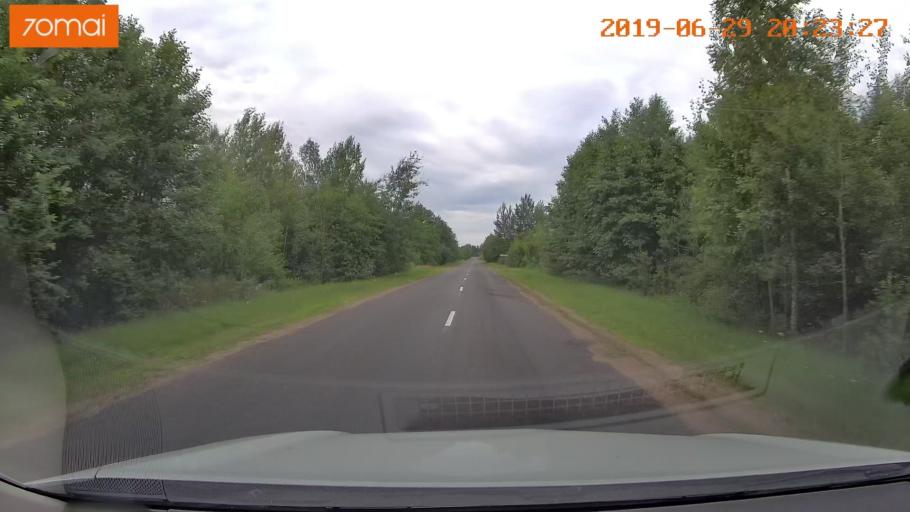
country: BY
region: Brest
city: Asnyezhytsy
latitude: 52.4448
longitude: 26.2607
